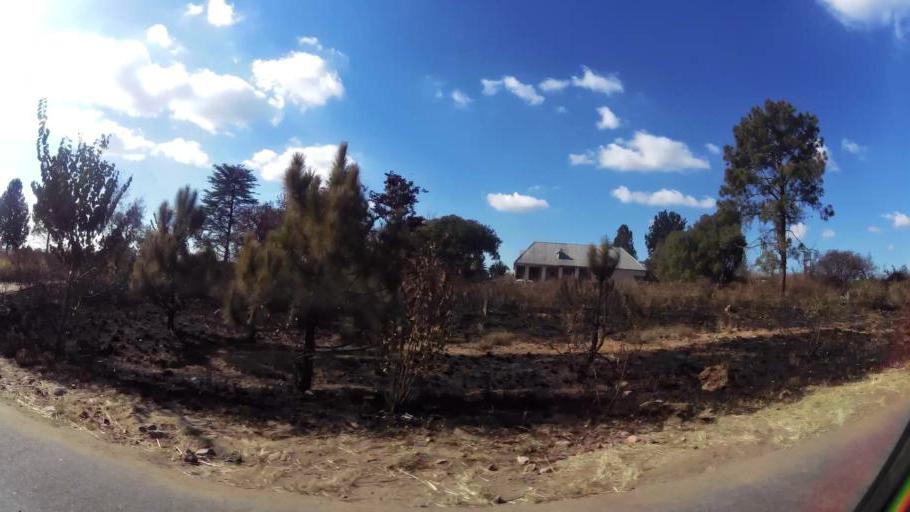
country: ZA
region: Gauteng
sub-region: West Rand District Municipality
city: Muldersdriseloop
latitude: -26.0449
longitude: 27.9078
